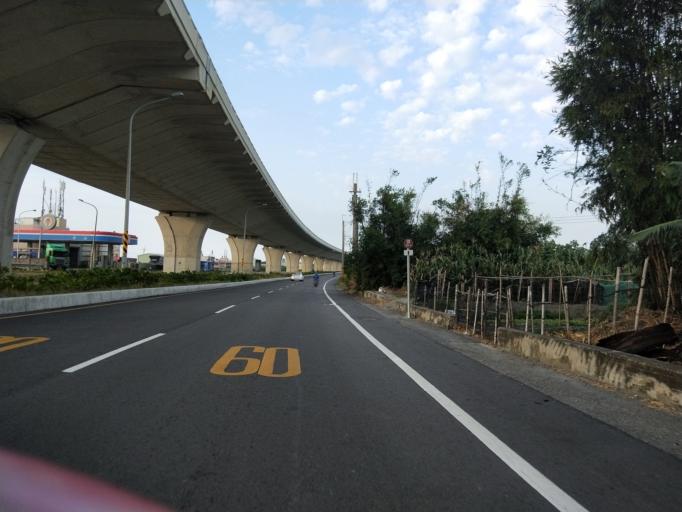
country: TW
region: Taiwan
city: Fengyuan
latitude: 24.4111
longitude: 120.6158
